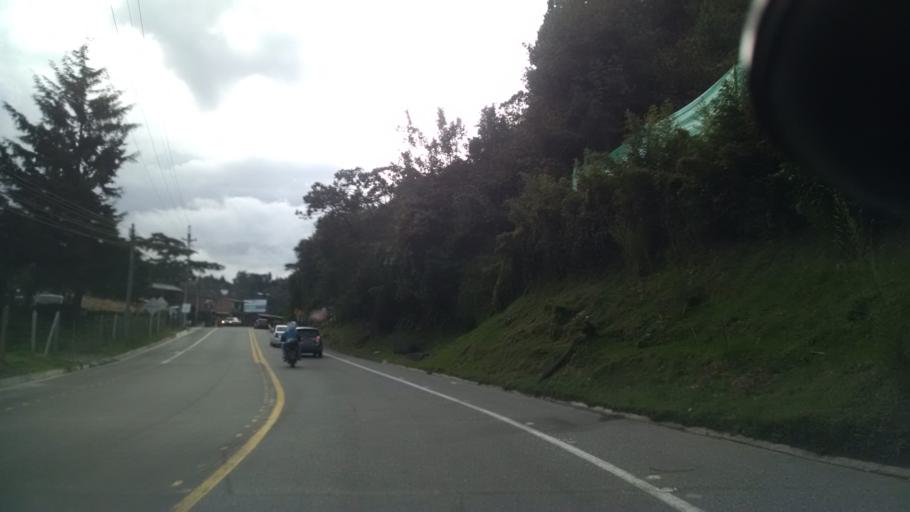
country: CO
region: Antioquia
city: El Retiro
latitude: 6.1387
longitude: -75.5106
